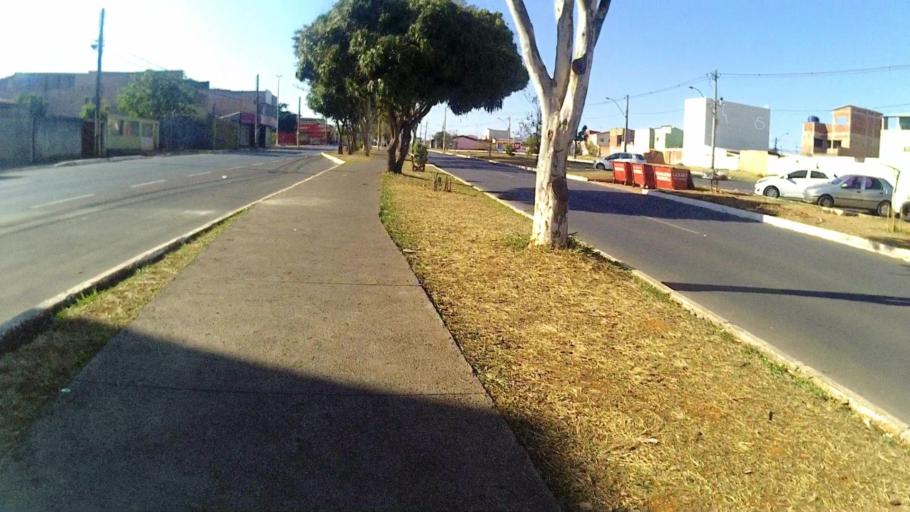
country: BR
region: Federal District
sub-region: Brasilia
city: Brasilia
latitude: -15.9012
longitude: -48.0507
